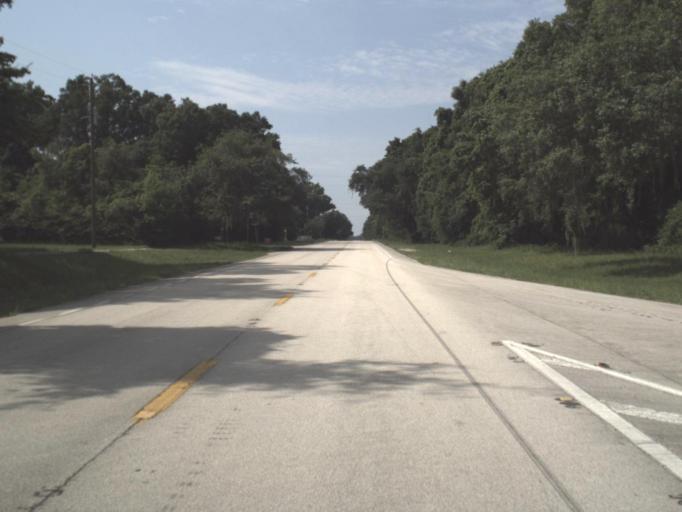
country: US
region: Florida
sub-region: Bradford County
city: Starke
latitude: 29.9585
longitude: -82.0164
